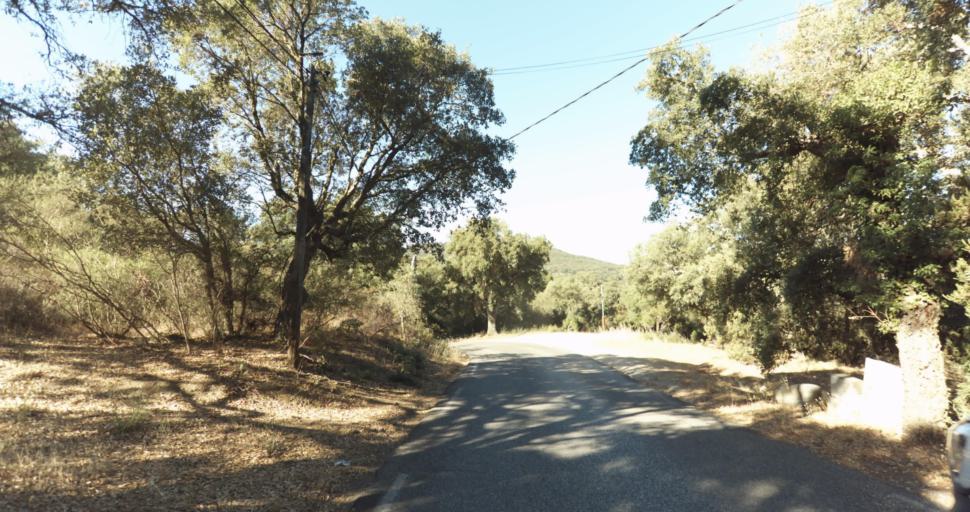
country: FR
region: Provence-Alpes-Cote d'Azur
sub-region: Departement du Var
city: Gassin
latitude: 43.2178
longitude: 6.5853
